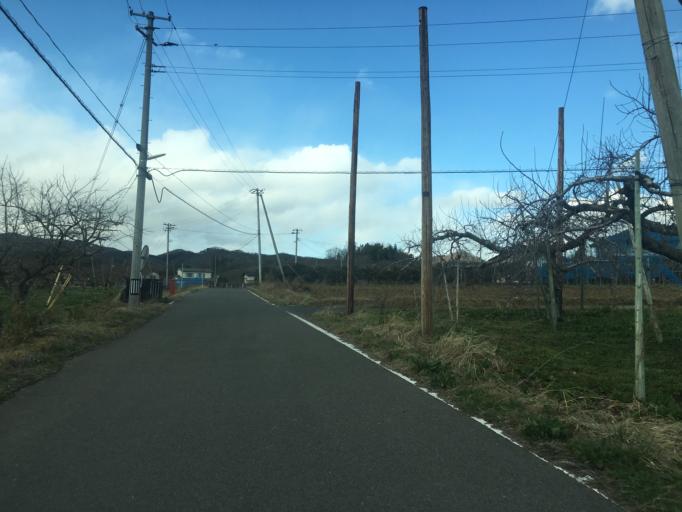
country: JP
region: Fukushima
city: Yanagawamachi-saiwaicho
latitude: 37.8781
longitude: 140.5971
